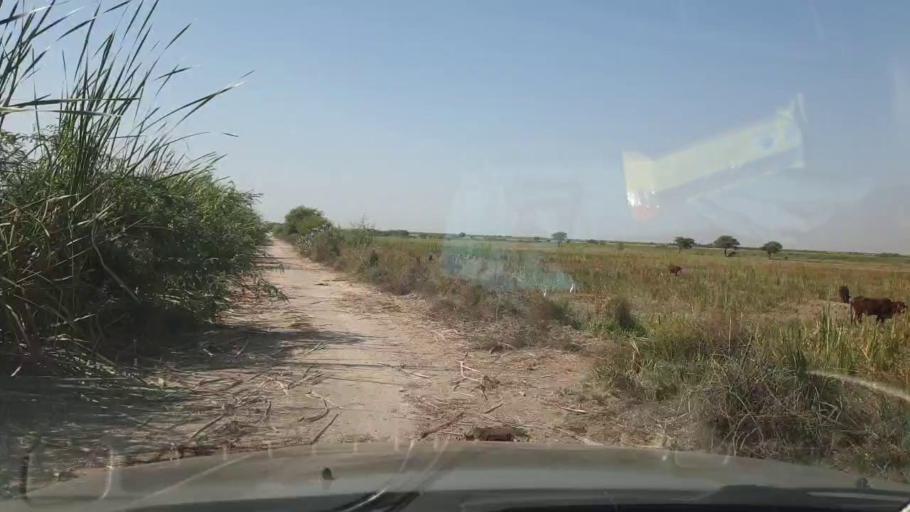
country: PK
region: Sindh
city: Daro Mehar
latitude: 24.9742
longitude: 68.1103
